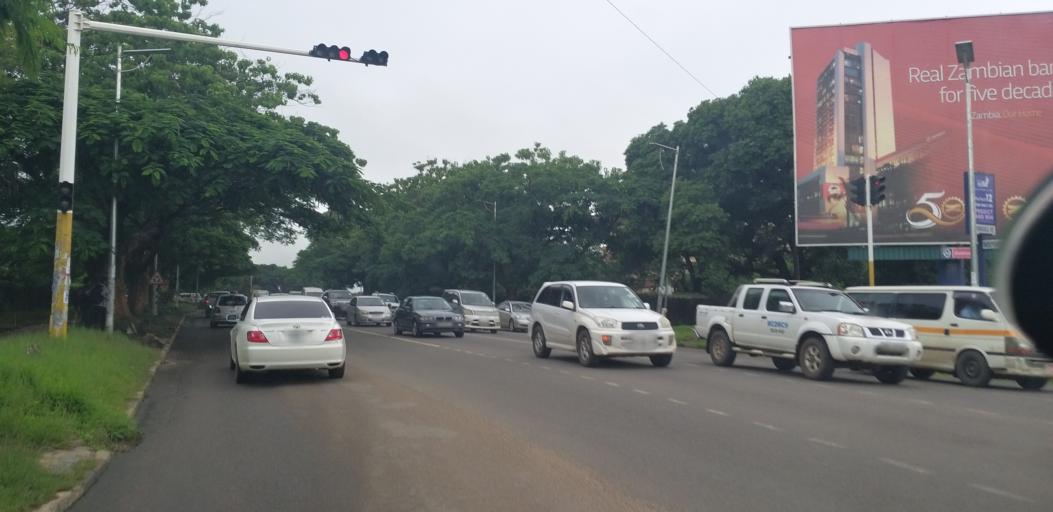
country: ZM
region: Lusaka
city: Lusaka
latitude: -15.4197
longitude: 28.3030
